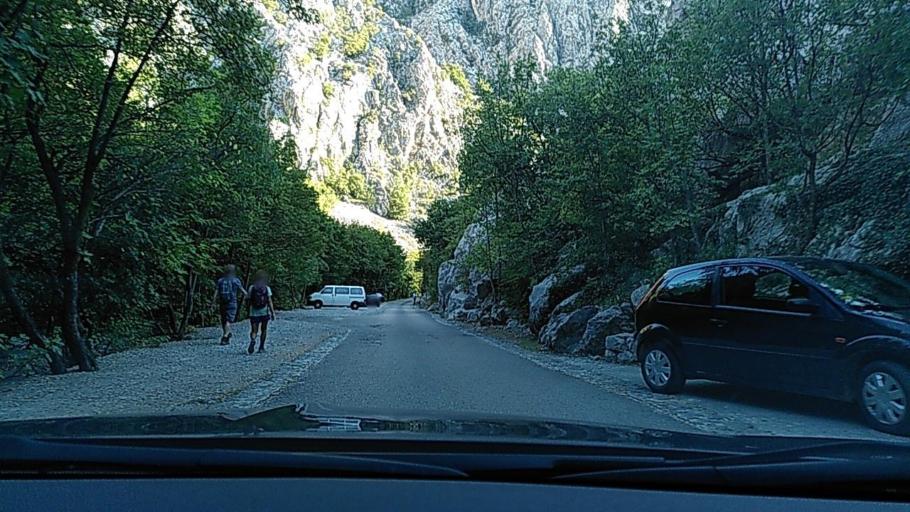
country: HR
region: Zadarska
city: Starigrad
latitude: 44.3001
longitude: 15.4699
